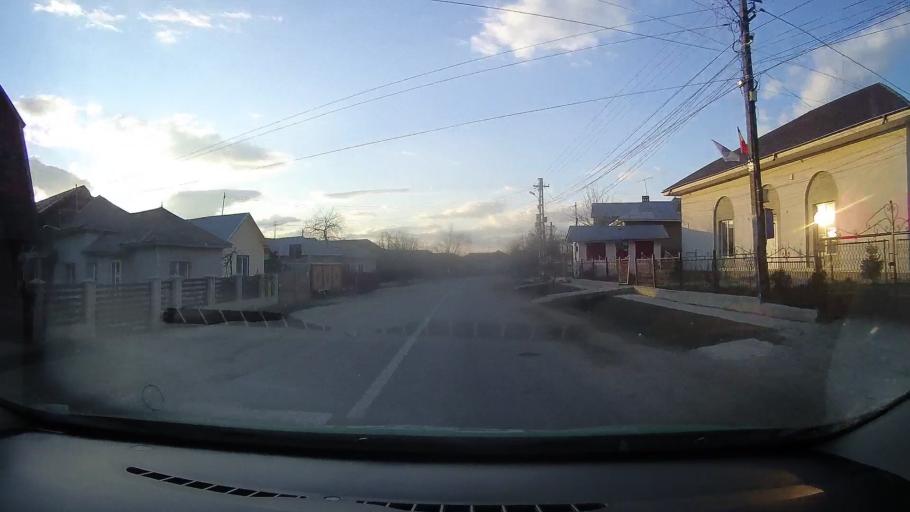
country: RO
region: Dambovita
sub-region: Comuna Gura Ocnitei
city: Adanca
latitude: 44.9207
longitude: 25.6140
